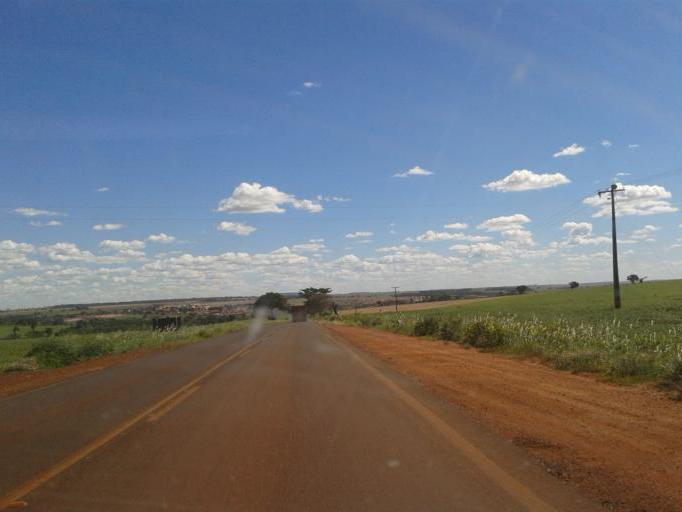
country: BR
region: Minas Gerais
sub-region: Capinopolis
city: Capinopolis
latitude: -18.6596
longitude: -49.5560
